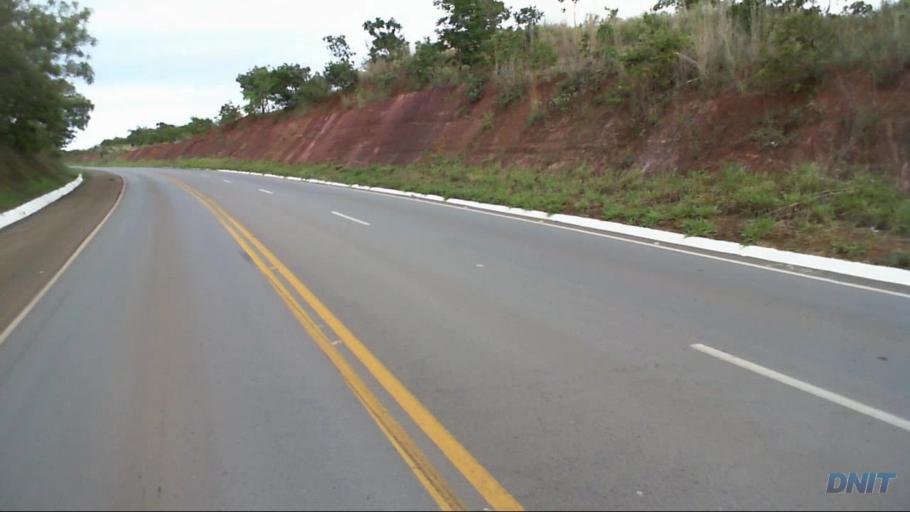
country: BR
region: Goias
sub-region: Barro Alto
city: Barro Alto
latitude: -14.8688
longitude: -49.0087
